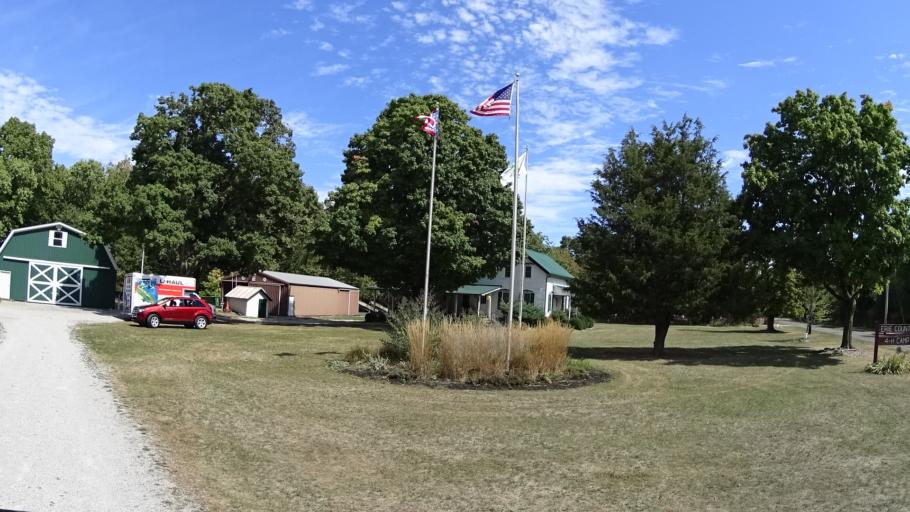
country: US
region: Ohio
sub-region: Erie County
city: Sandusky
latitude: 41.6072
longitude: -82.6979
